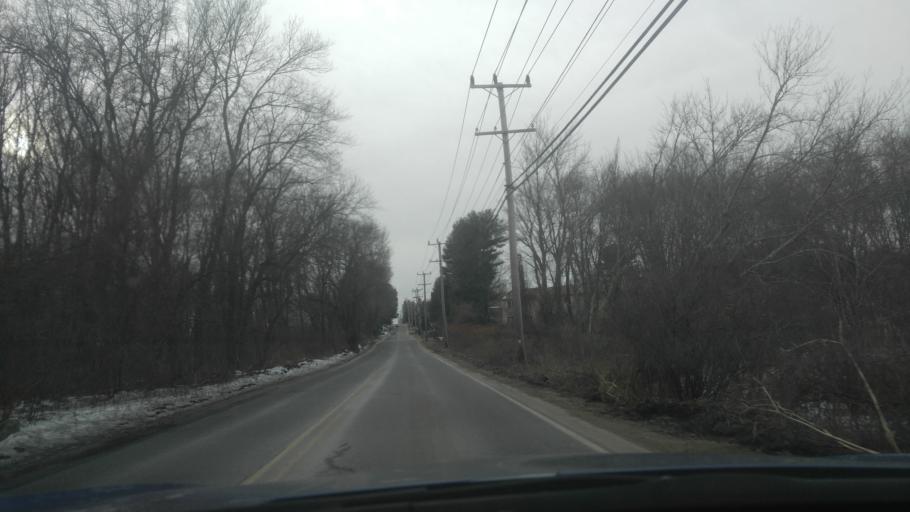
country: US
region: Rhode Island
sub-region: Kent County
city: West Warwick
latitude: 41.6736
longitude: -71.5065
